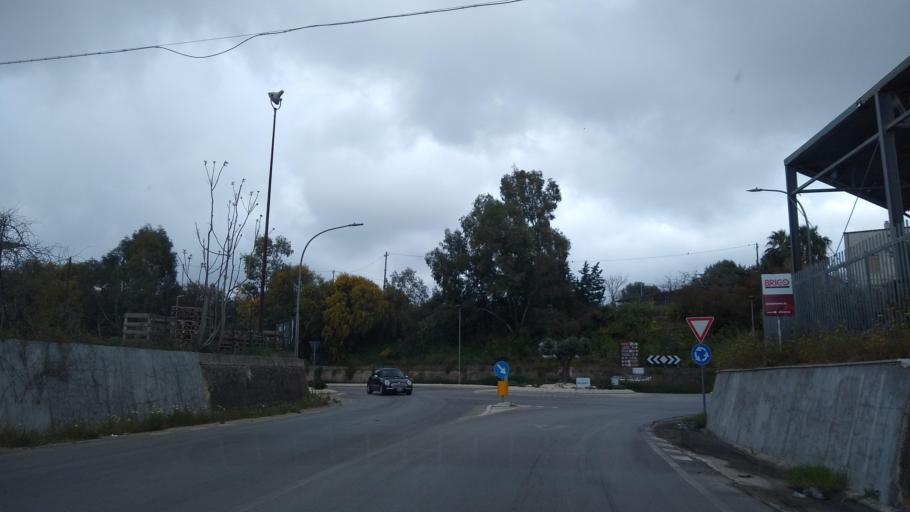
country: IT
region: Sicily
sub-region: Trapani
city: Alcamo
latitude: 37.9930
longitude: 12.9600
